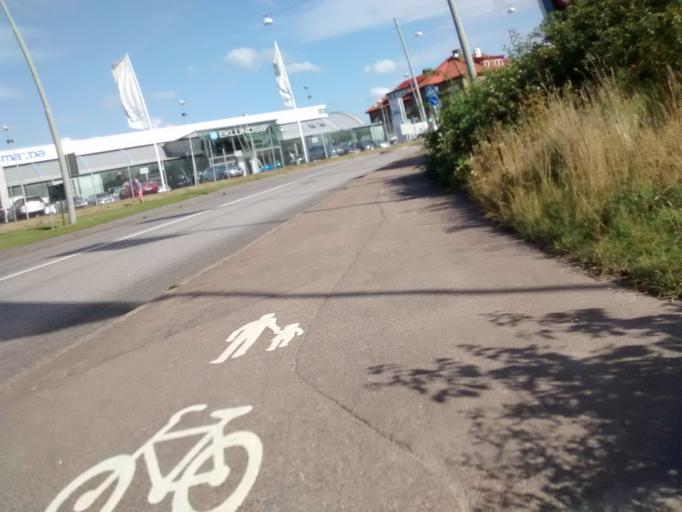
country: SE
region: Vaestra Goetaland
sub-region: Goteborg
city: Goeteborg
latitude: 57.7203
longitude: 11.9626
